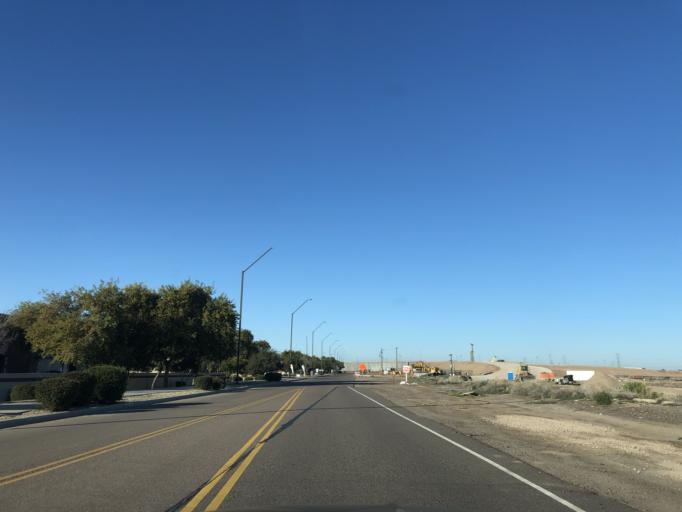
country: US
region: Arizona
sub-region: Maricopa County
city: Avondale
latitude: 33.4530
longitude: -112.3238
